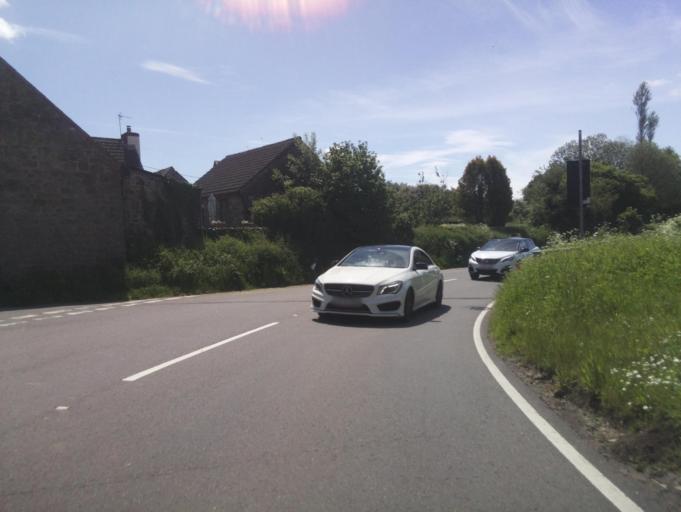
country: GB
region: Wales
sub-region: Monmouthshire
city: Mitchel Troy
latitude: 51.7437
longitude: -2.7246
